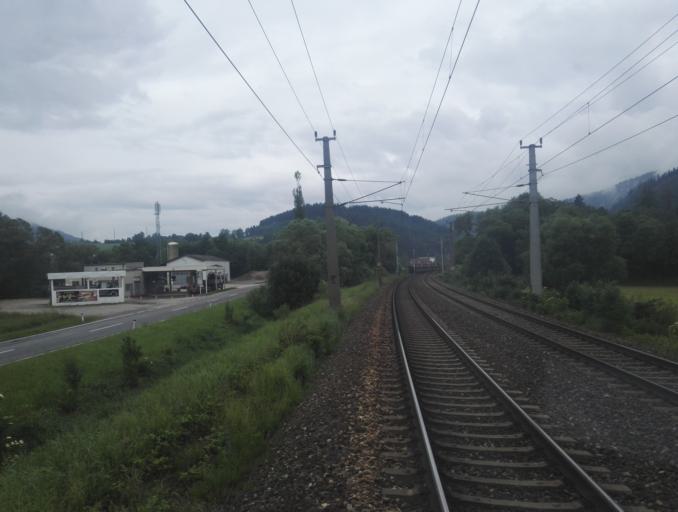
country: AT
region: Styria
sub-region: Politischer Bezirk Bruck-Muerzzuschlag
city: Mitterdorf im Muerztal
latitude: 47.5285
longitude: 15.4914
